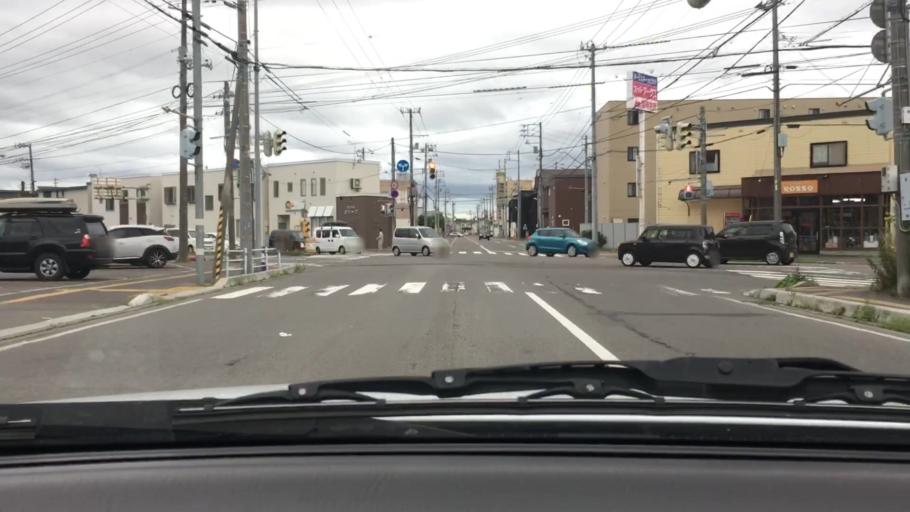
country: JP
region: Hokkaido
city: Hakodate
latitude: 41.8010
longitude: 140.7302
